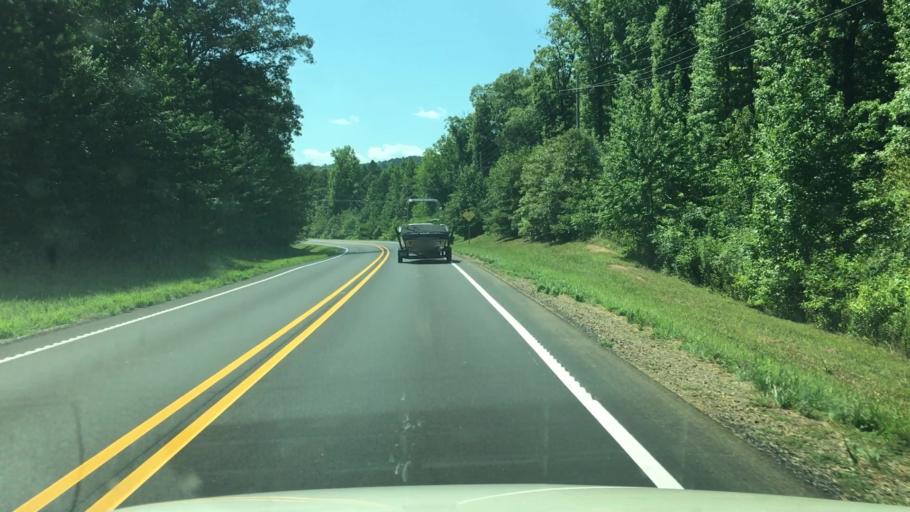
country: US
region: Arkansas
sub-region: Garland County
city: Rockwell
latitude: 34.5231
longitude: -93.3290
